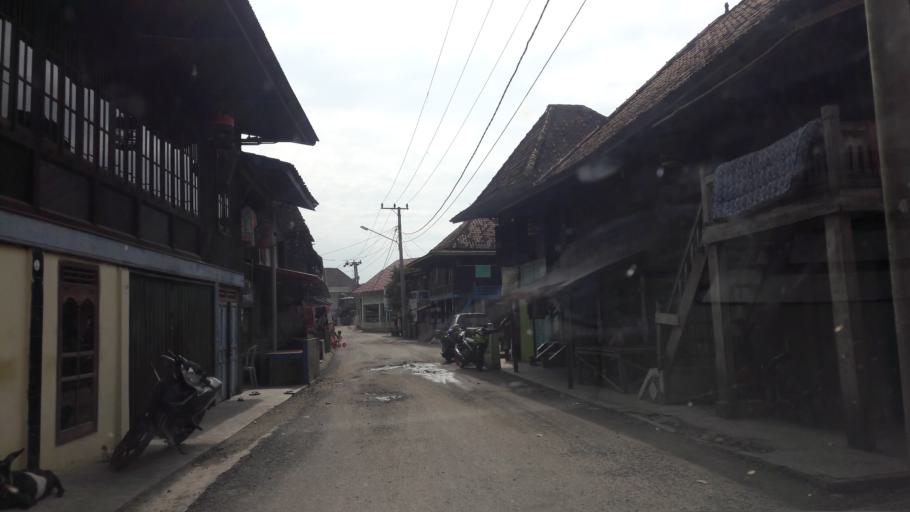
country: ID
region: South Sumatra
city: Gunungmenang
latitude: -3.0900
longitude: 104.0235
